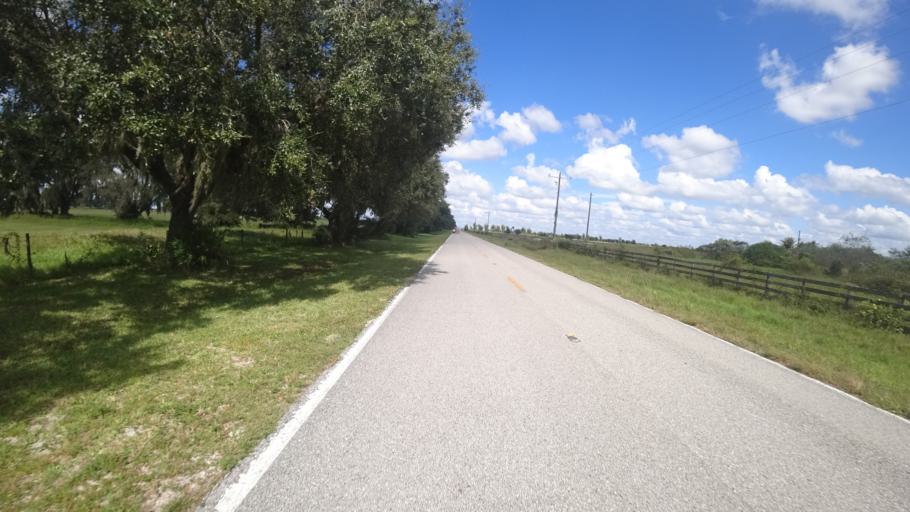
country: US
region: Florida
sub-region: Sarasota County
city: Warm Mineral Springs
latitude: 27.2884
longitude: -82.1921
